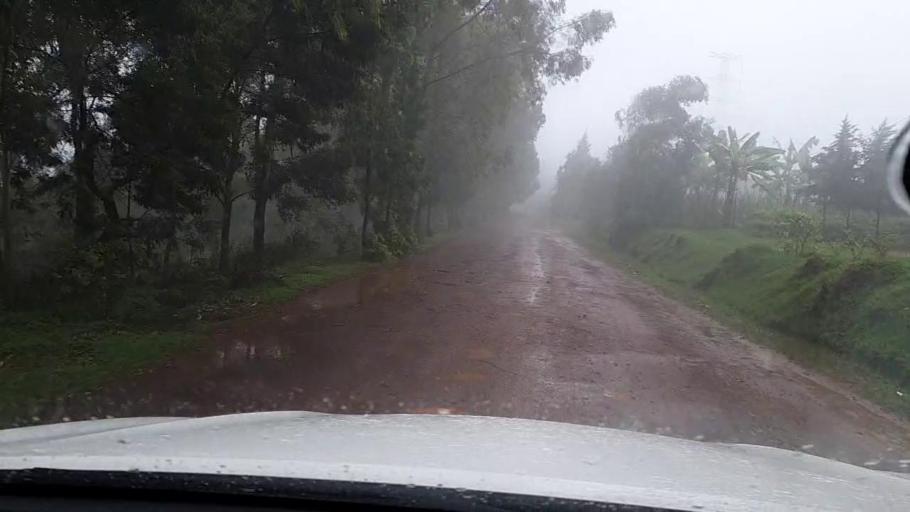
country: RW
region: Kigali
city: Kigali
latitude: -1.7716
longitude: 29.9985
